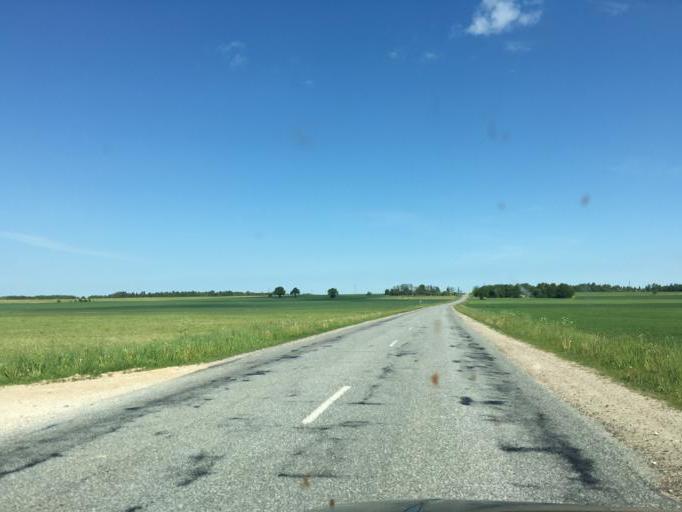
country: LV
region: Talsu Rajons
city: Valdemarpils
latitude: 57.3488
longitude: 22.4986
